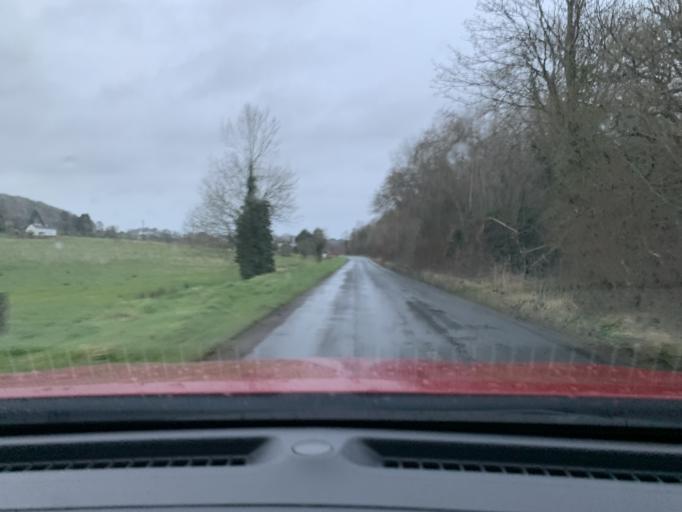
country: IE
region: Connaught
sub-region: Roscommon
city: Boyle
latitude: 54.0453
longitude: -8.3359
